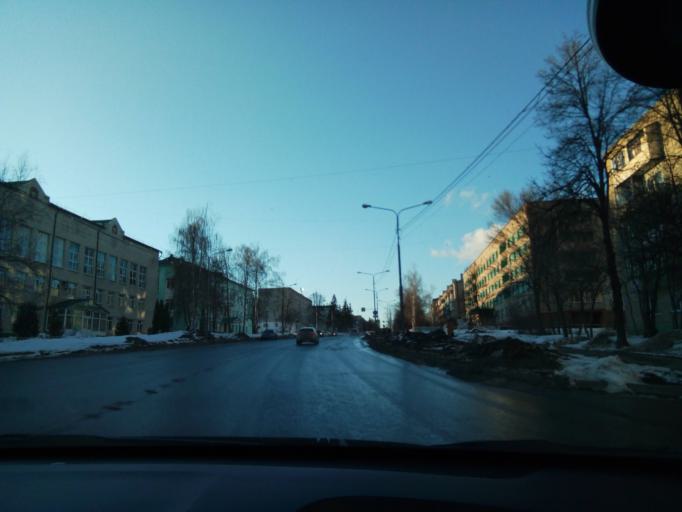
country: RU
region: Chuvashia
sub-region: Cheboksarskiy Rayon
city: Cheboksary
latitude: 56.1381
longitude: 47.2016
